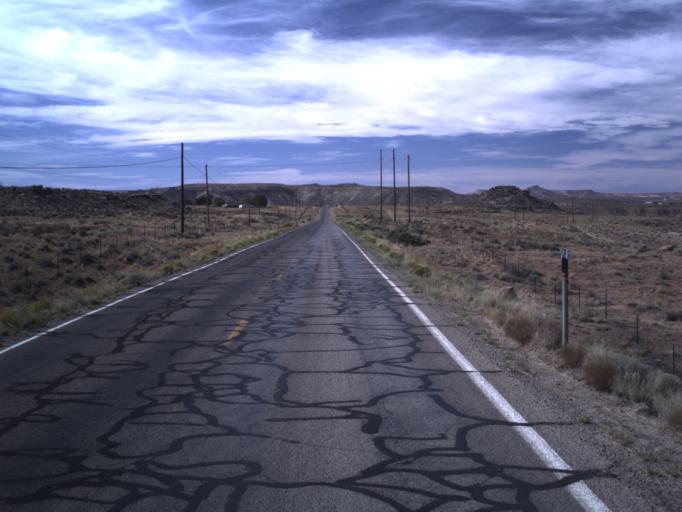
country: US
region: Utah
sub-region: San Juan County
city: Blanding
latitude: 37.2831
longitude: -109.2928
